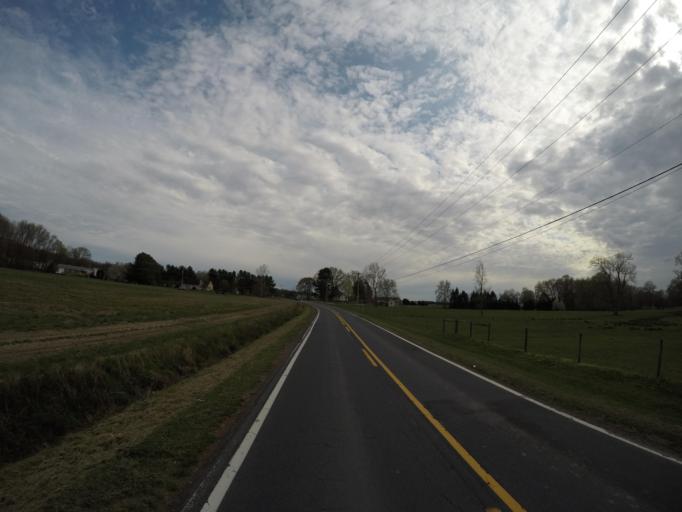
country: US
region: Delaware
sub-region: New Castle County
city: Glasgow
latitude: 39.5630
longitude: -75.7632
